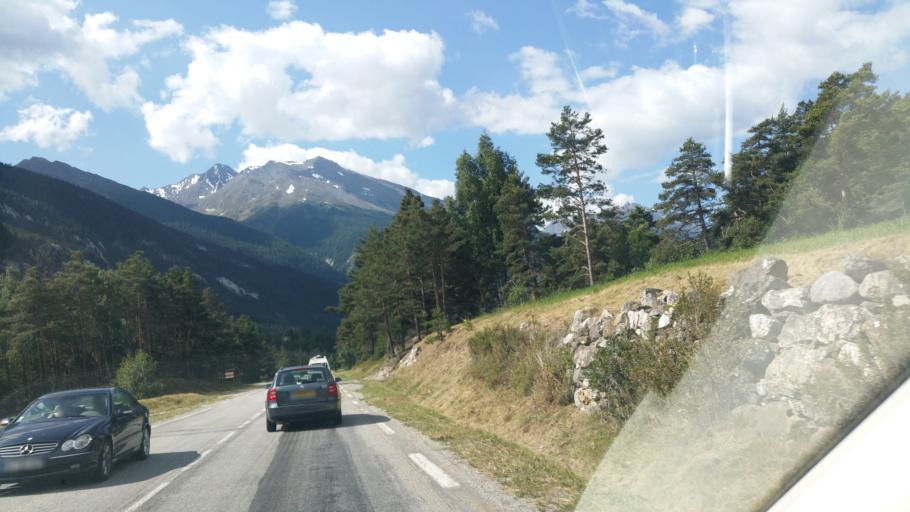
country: FR
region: Rhone-Alpes
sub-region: Departement de la Savoie
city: Modane
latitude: 45.2493
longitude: 6.7978
